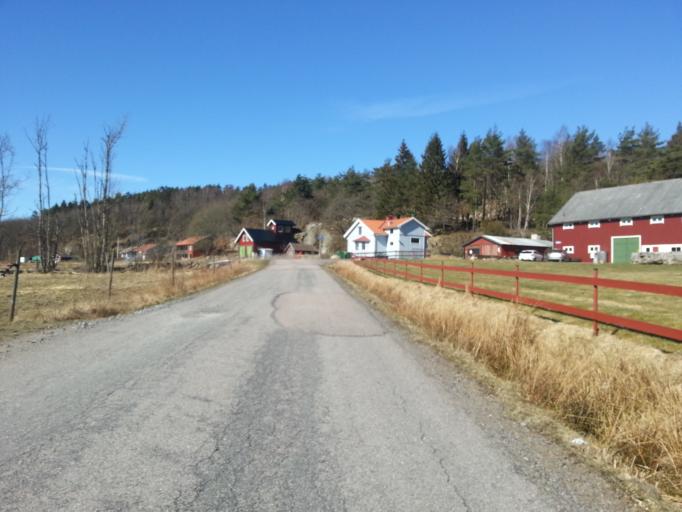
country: SE
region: Vaestra Goetaland
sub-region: Kungalvs Kommun
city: Kungalv
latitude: 57.8996
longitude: 11.9722
